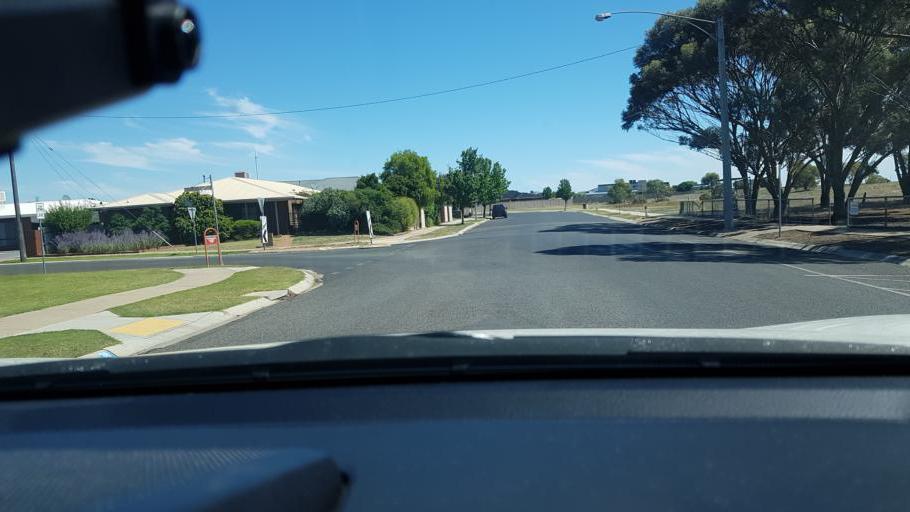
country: AU
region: Victoria
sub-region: Horsham
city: Horsham
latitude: -36.7118
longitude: 142.1831
